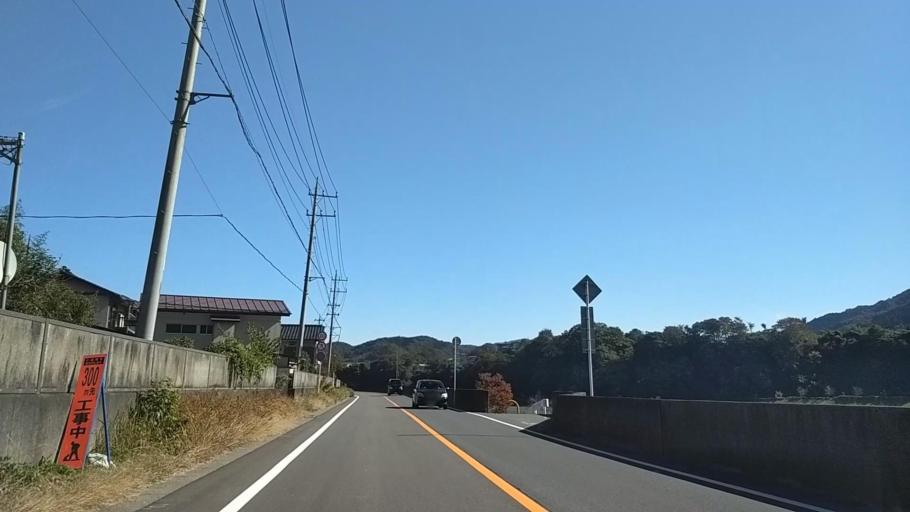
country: JP
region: Yamanashi
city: Uenohara
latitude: 35.6167
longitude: 139.1108
